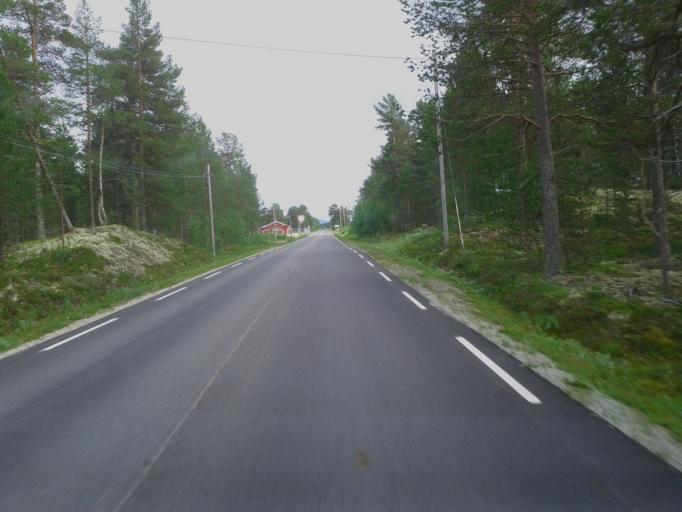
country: NO
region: Sor-Trondelag
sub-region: Roros
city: Roros
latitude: 62.2883
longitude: 11.7332
